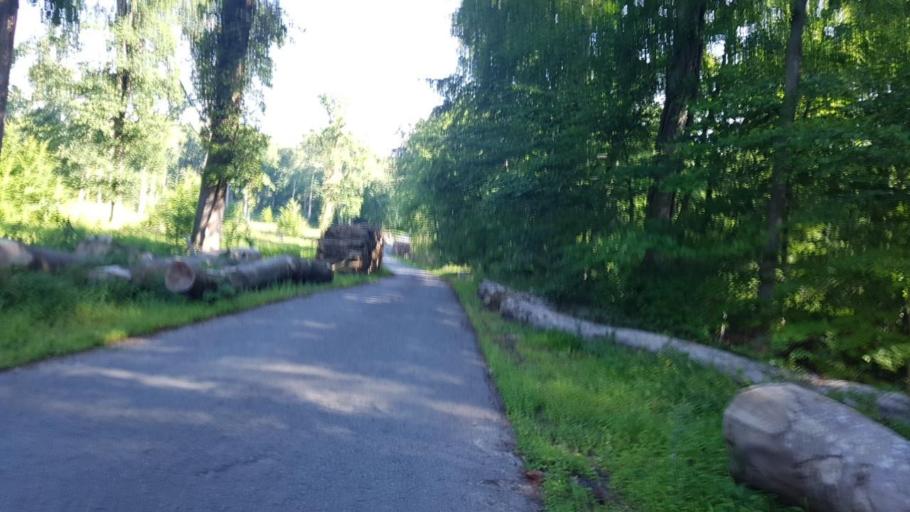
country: FR
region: Picardie
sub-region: Departement de l'Oise
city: Fleurines
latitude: 49.2642
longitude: 2.6182
